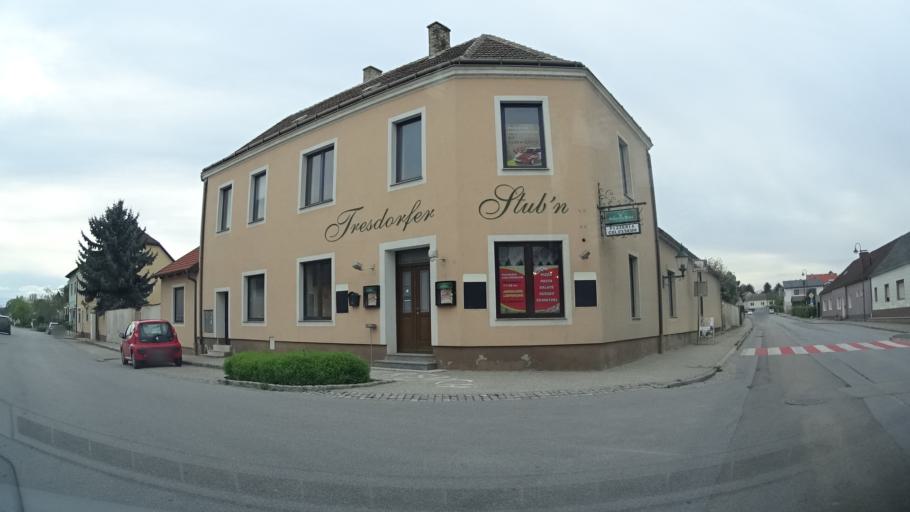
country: AT
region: Lower Austria
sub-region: Politischer Bezirk Korneuburg
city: Harmannsdorf
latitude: 48.3807
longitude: 16.3577
